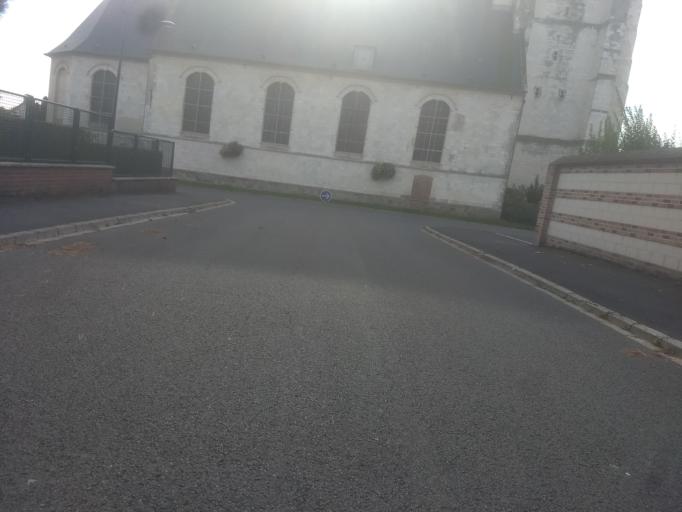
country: FR
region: Nord-Pas-de-Calais
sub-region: Departement du Pas-de-Calais
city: Dainville
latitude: 50.2818
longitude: 2.7229
